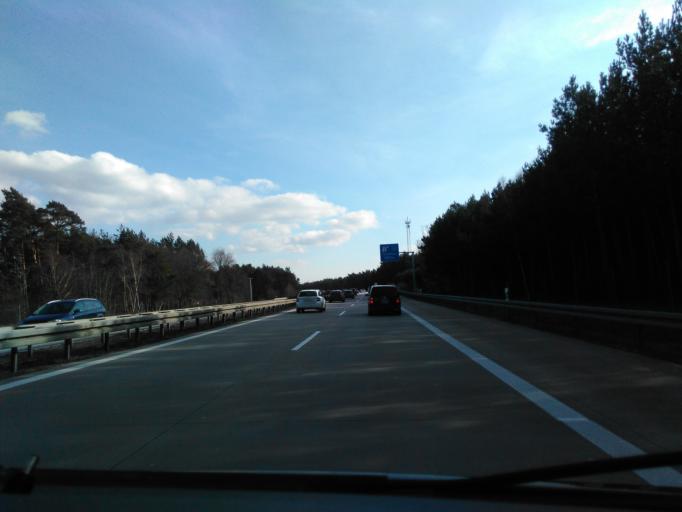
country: DE
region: Brandenburg
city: Kasel-Golzig
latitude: 52.0229
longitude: 13.6848
